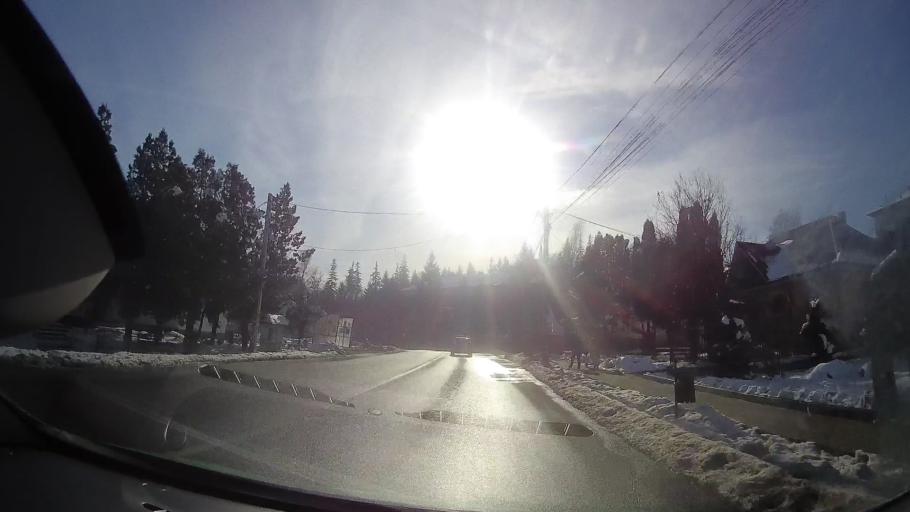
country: RO
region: Neamt
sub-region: Comuna Baltatesti
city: Baltatesti
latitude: 47.1213
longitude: 26.3098
